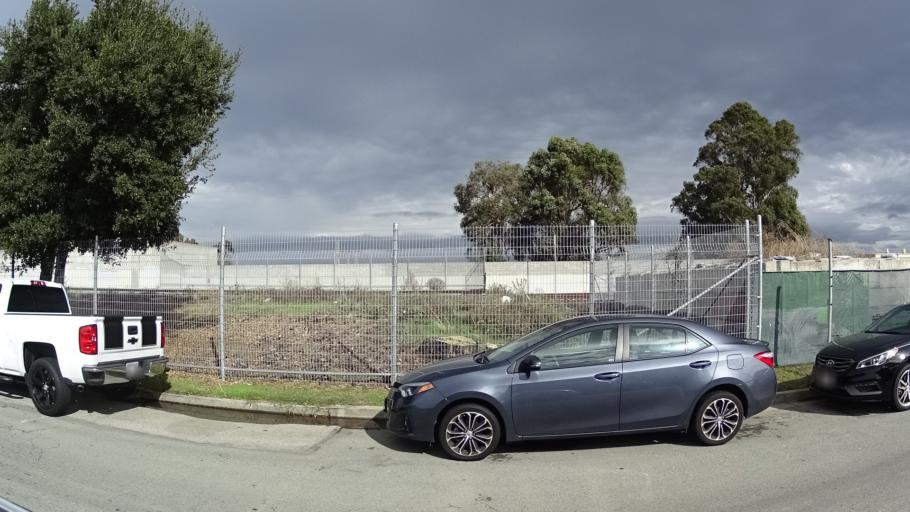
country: US
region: California
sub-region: San Mateo County
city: San Bruno
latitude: 37.6204
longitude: -122.4059
